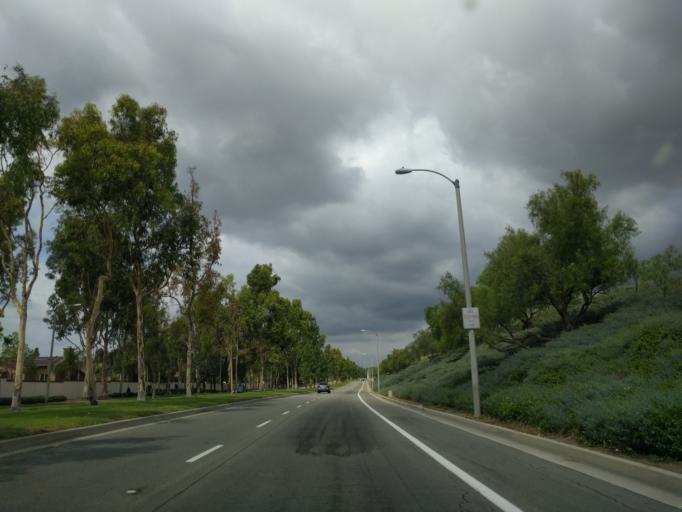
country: US
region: California
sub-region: Orange County
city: North Tustin
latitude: 33.7515
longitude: -117.7662
